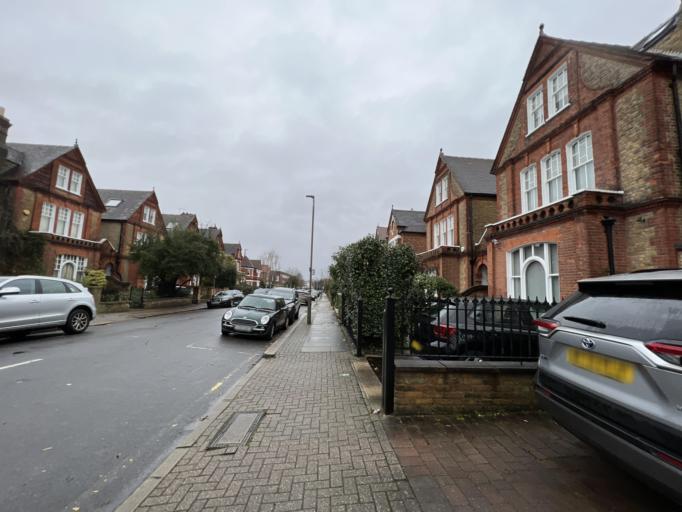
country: GB
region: England
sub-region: Greater London
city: Wandsworth
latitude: 51.4616
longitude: -0.2282
